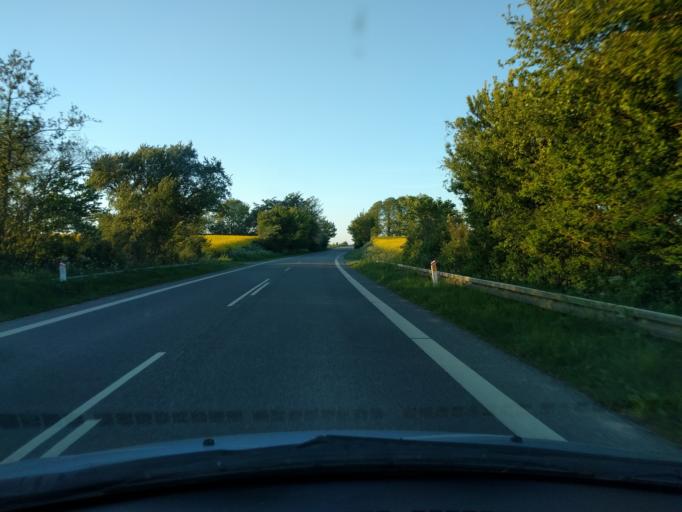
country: DK
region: Zealand
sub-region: Guldborgsund Kommune
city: Stubbekobing
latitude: 54.8774
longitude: 12.0285
